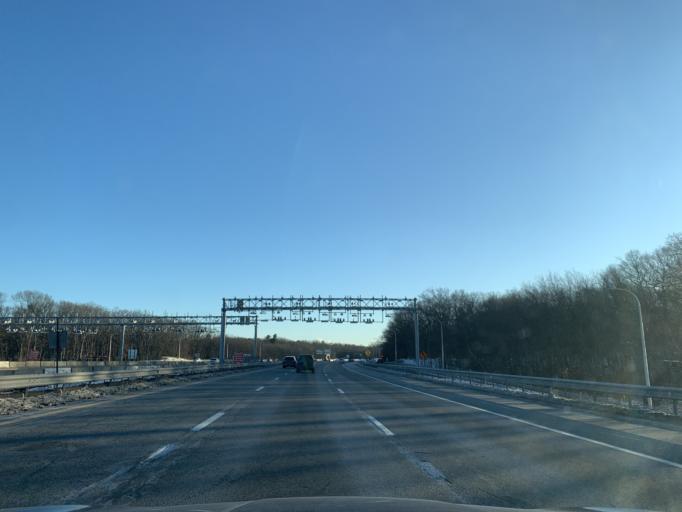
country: US
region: Rhode Island
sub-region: Providence County
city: Johnston
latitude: 41.8491
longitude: -71.5115
